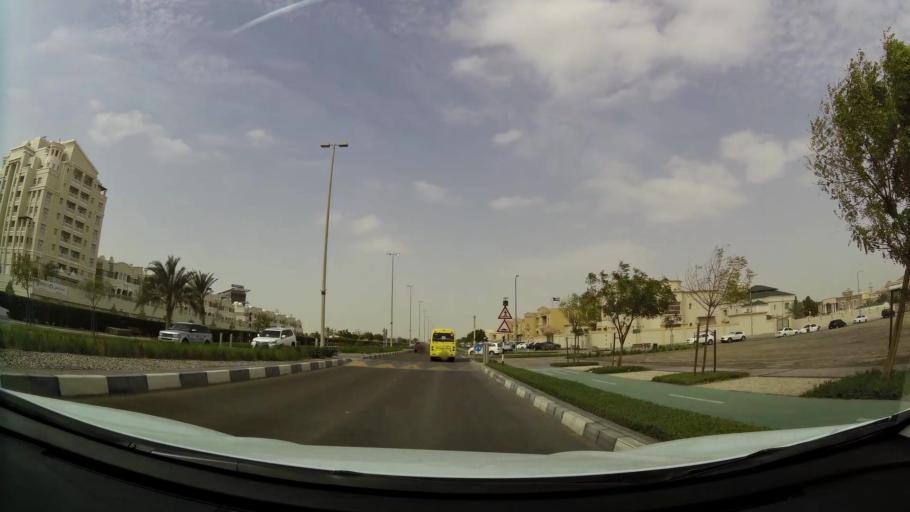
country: AE
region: Abu Dhabi
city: Abu Dhabi
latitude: 24.4049
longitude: 54.5521
